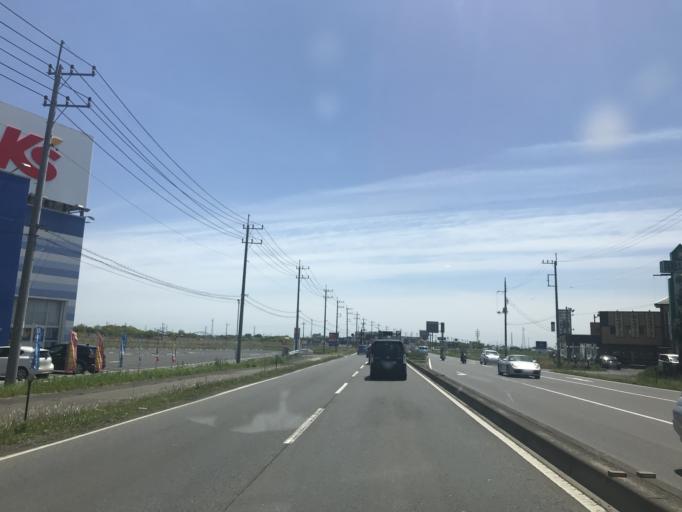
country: JP
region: Ibaraki
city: Ishige
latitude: 36.1979
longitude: 139.9855
